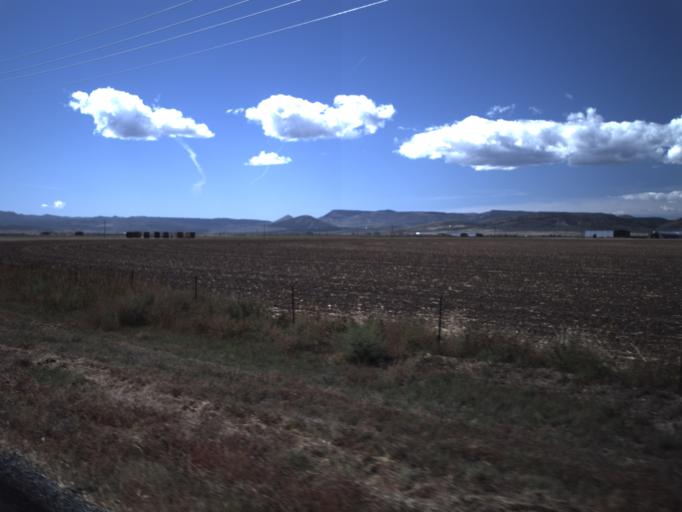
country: US
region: Utah
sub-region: Washington County
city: Enterprise
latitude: 37.6527
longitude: -113.6612
